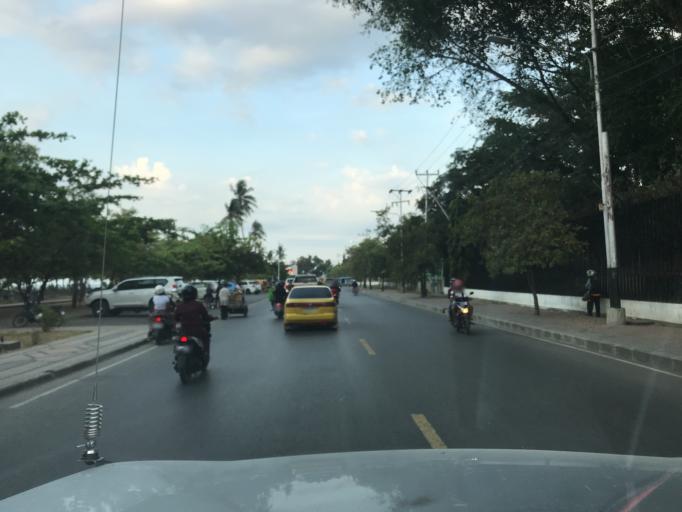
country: TL
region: Dili
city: Dili
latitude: -8.5512
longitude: 125.5833
